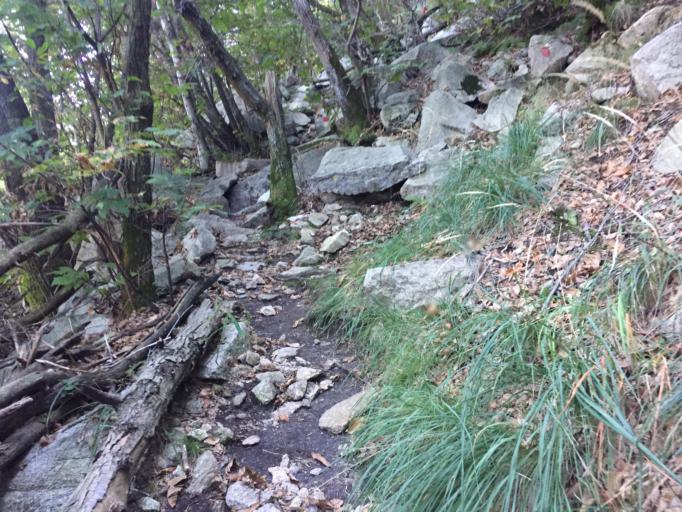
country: IT
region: Piedmont
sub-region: Provincia Verbano-Cusio-Ossola
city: Mergozzo
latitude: 45.9456
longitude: 8.4596
